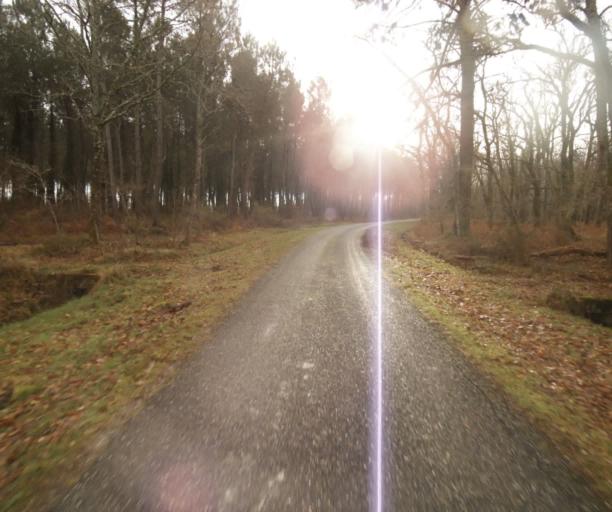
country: FR
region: Aquitaine
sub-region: Departement des Landes
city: Gabarret
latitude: 44.0766
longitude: 0.0810
